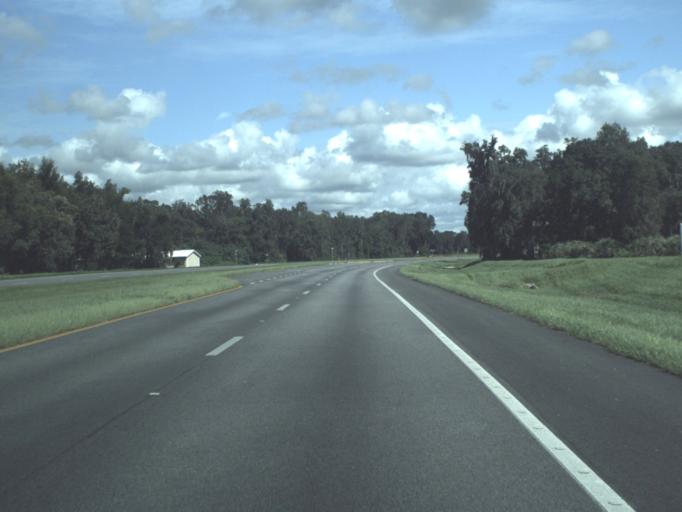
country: US
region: Florida
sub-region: Hillsborough County
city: Plant City
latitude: 28.0387
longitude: -82.1349
